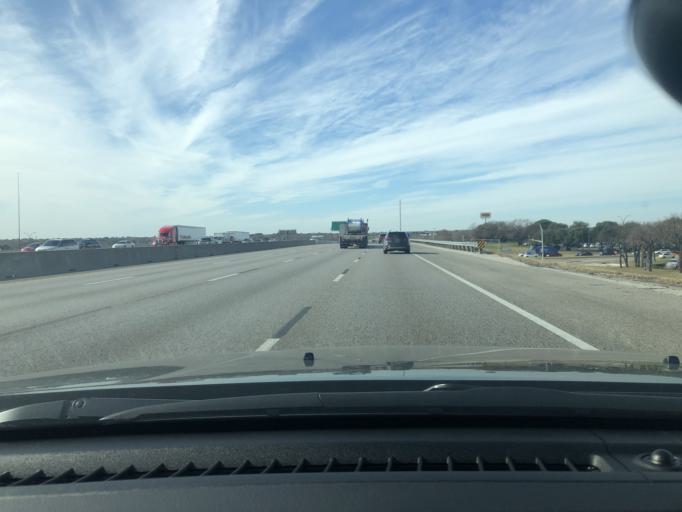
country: US
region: Texas
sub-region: Tarrant County
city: Dalworthington Gardens
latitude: 32.6747
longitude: -97.1477
